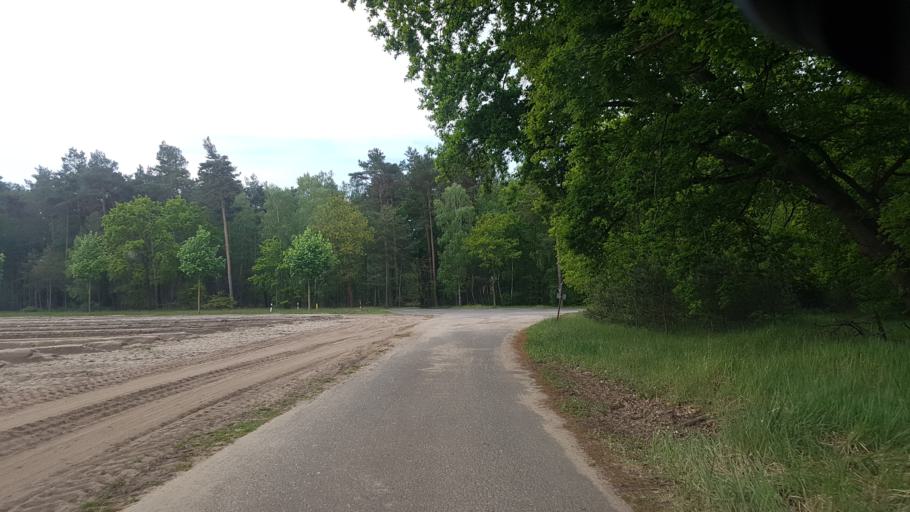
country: DE
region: Brandenburg
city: Luckenwalde
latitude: 52.1101
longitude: 13.0563
